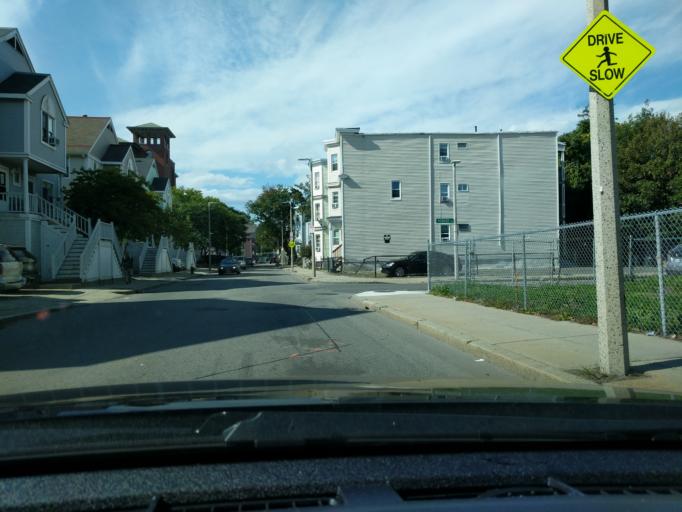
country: US
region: Massachusetts
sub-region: Suffolk County
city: South Boston
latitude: 42.3131
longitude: -71.0753
